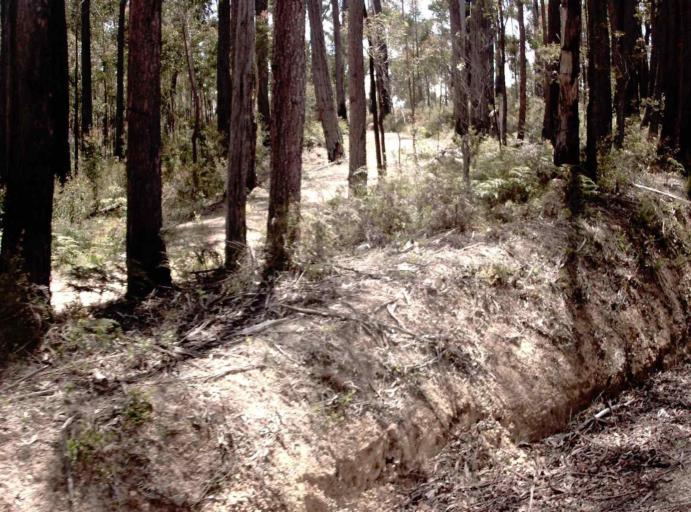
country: AU
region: New South Wales
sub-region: Bombala
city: Bombala
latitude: -37.5683
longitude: 148.9442
